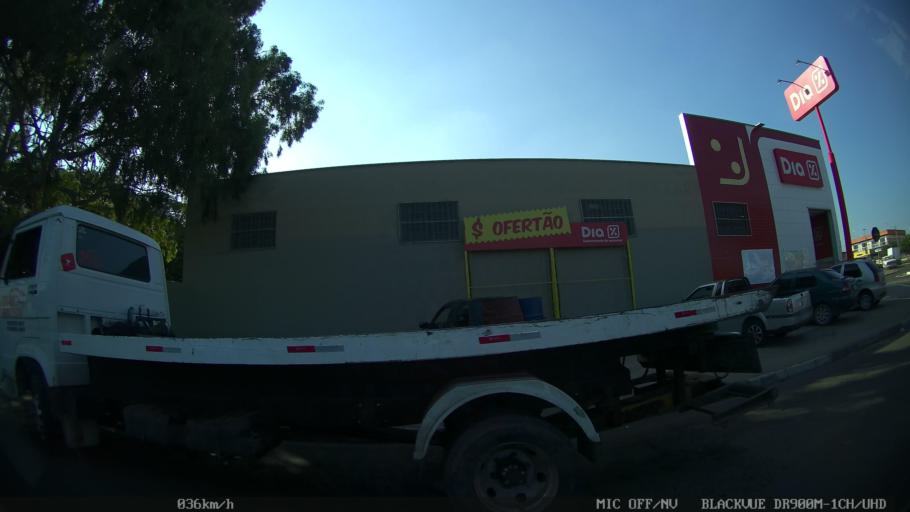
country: BR
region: Sao Paulo
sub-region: Campinas
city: Campinas
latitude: -22.9886
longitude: -47.1424
